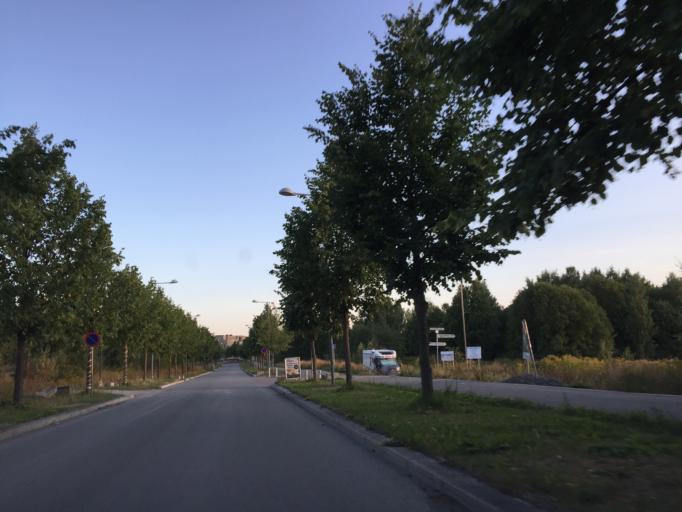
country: NO
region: Akershus
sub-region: Baerum
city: Lysaker
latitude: 59.8972
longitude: 10.6087
